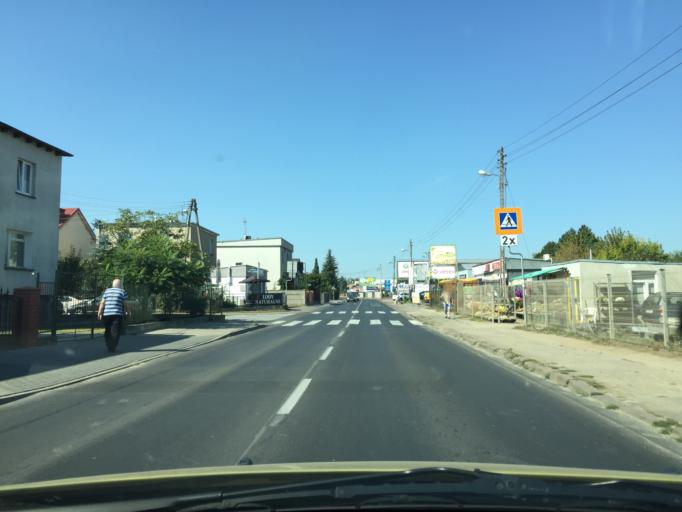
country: PL
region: Greater Poland Voivodeship
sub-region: Powiat poznanski
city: Plewiska
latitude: 52.3864
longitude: 16.8192
